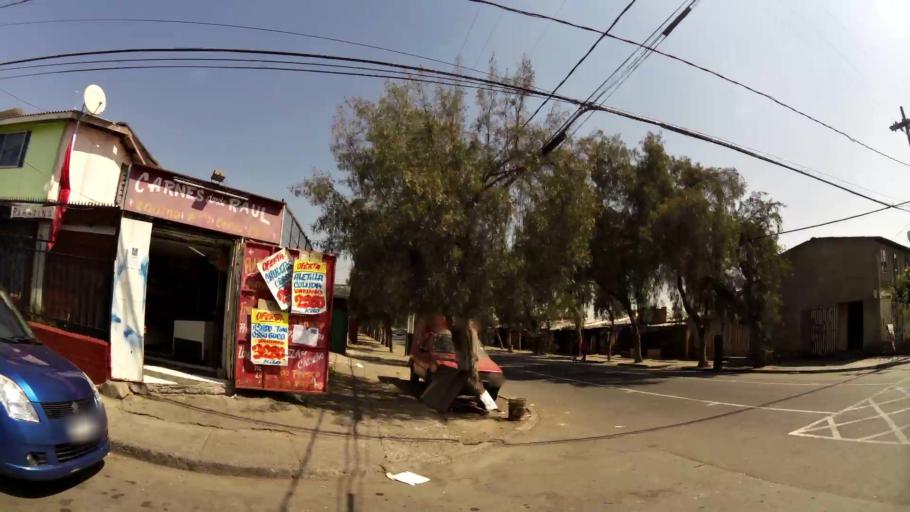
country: CL
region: Santiago Metropolitan
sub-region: Provincia de Santiago
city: La Pintana
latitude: -33.5602
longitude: -70.6131
